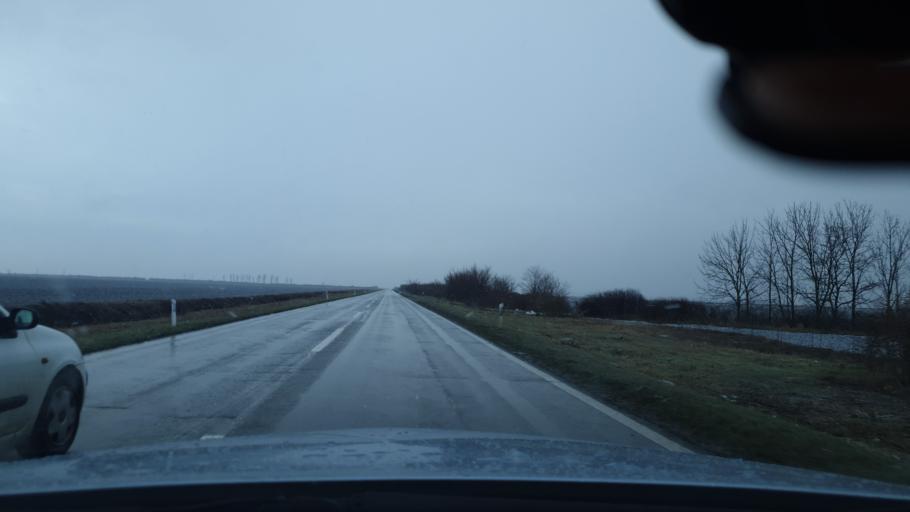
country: RS
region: Autonomna Pokrajina Vojvodina
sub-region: Juznobanatski Okrug
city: Pancevo
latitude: 44.8542
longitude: 20.7610
